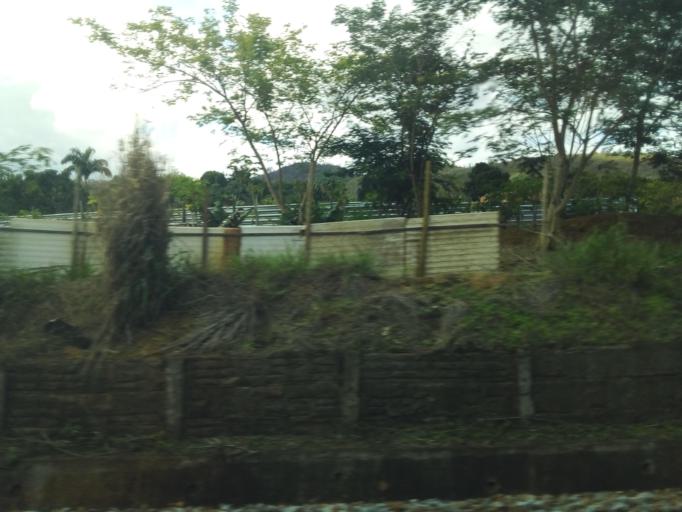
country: BR
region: Minas Gerais
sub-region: Governador Valadares
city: Governador Valadares
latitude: -18.9164
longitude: -42.0094
